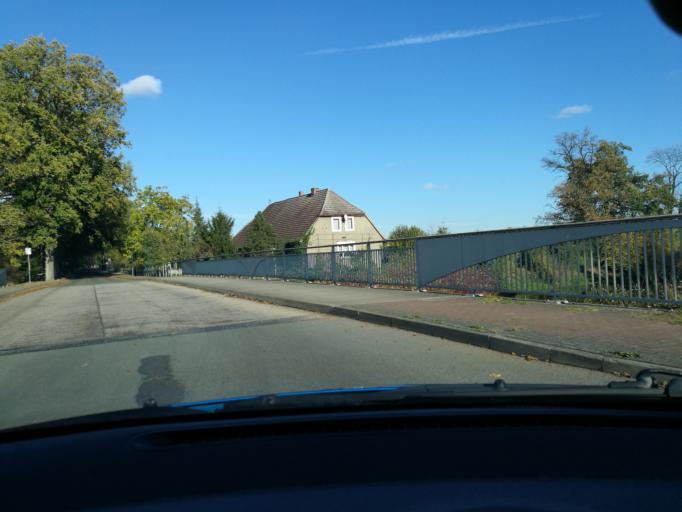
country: DE
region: Brandenburg
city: Lenzen
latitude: 53.1078
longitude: 11.4269
